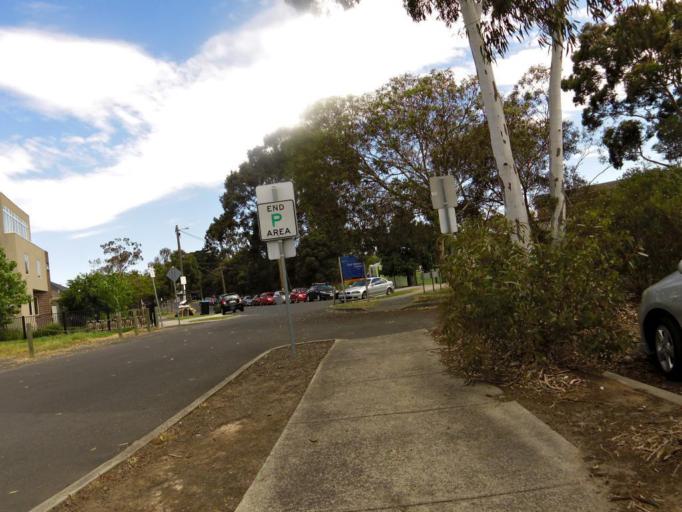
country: AU
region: Victoria
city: Carnegie
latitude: -37.8777
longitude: 145.0703
